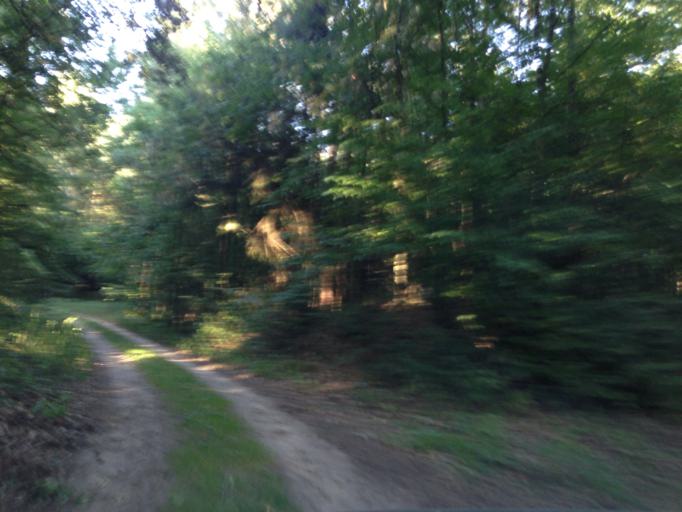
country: PL
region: Kujawsko-Pomorskie
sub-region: Powiat brodnicki
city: Gorzno
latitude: 53.2217
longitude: 19.7311
